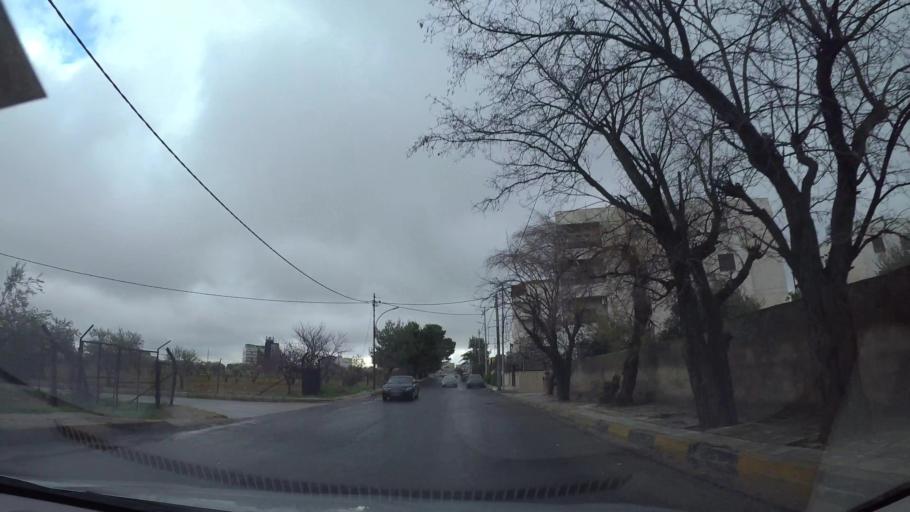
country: JO
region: Amman
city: Al Jubayhah
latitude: 32.0298
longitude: 35.8590
